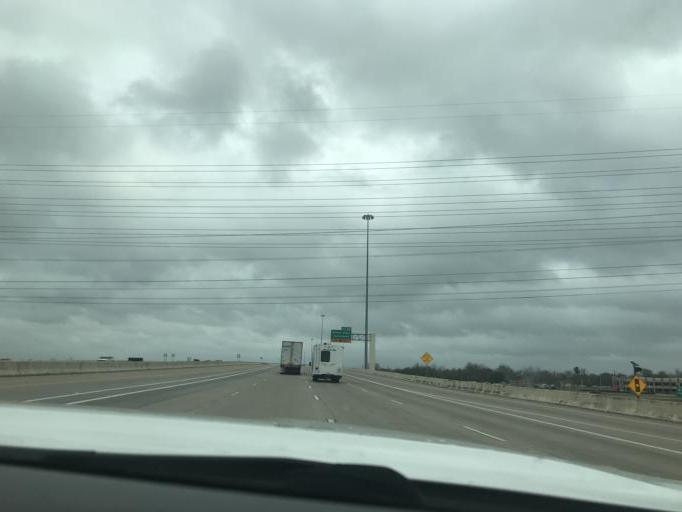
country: US
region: Texas
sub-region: Fort Bend County
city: Greatwood
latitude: 29.5604
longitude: -95.6938
